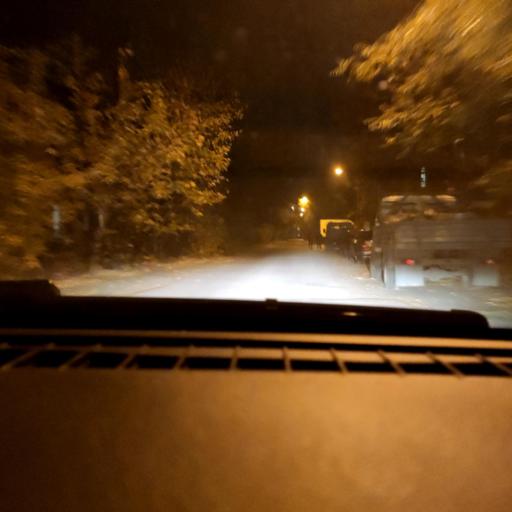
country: RU
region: Voronezj
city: Voronezh
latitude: 51.6324
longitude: 39.2399
